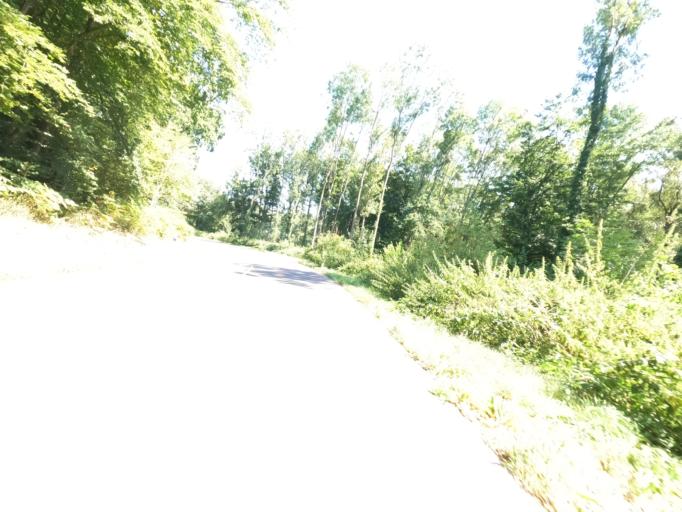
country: DE
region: North Rhine-Westphalia
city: Huckelhoven
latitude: 51.0908
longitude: 6.2093
